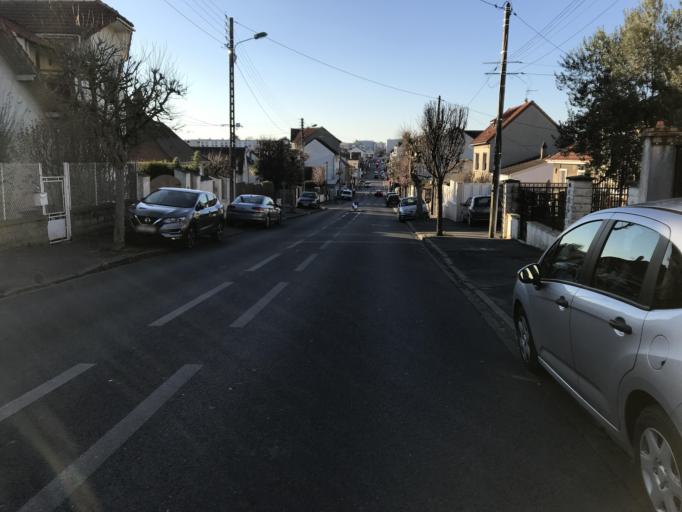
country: FR
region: Ile-de-France
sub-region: Departement de l'Essonne
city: Morangis
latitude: 48.6994
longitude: 2.3273
